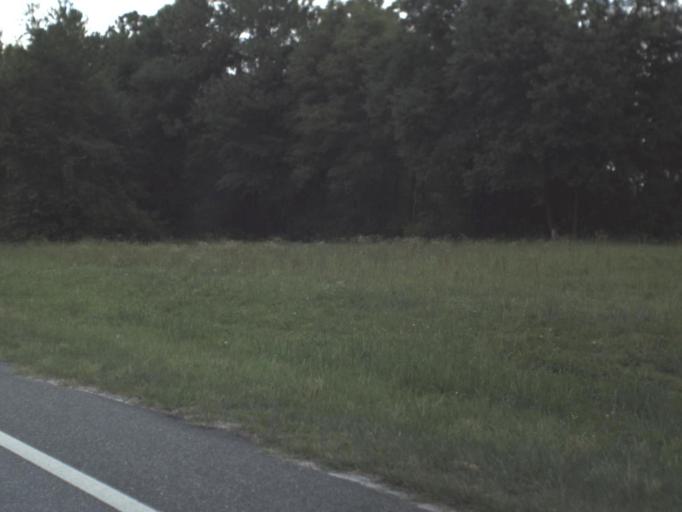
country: US
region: Georgia
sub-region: Echols County
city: Statenville
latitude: 30.5835
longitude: -83.0899
